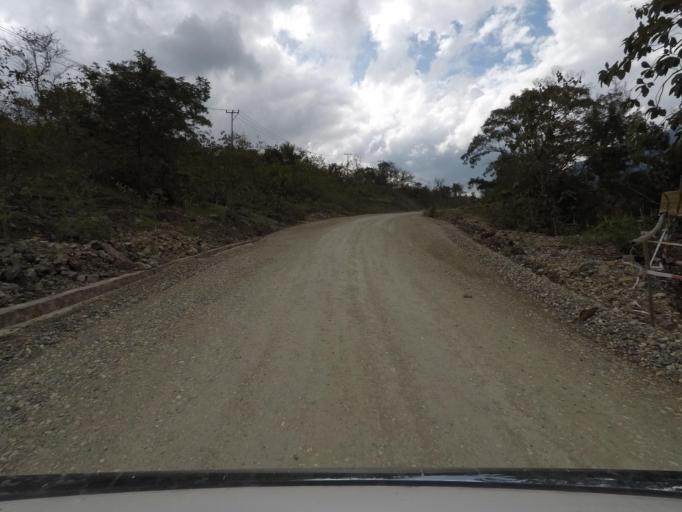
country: TL
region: Viqueque
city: Viqueque
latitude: -8.8136
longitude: 126.3814
